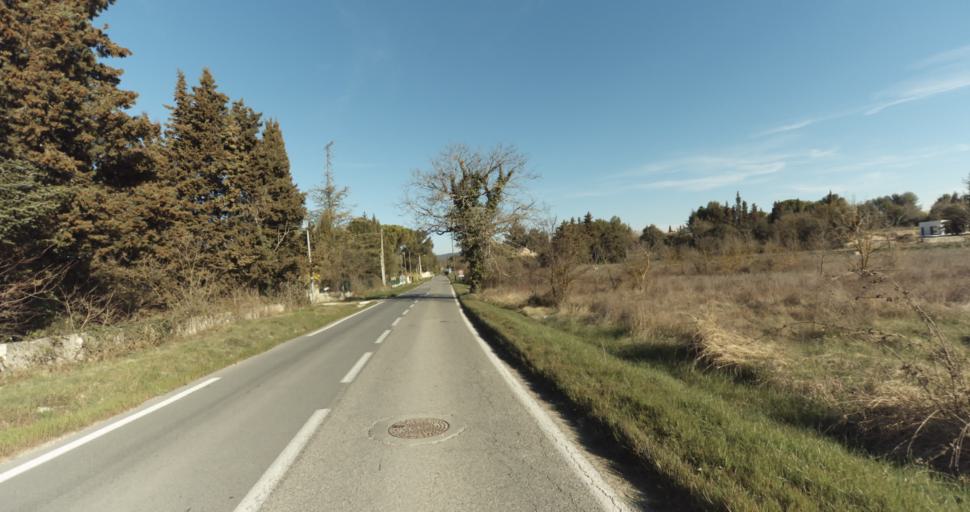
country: FR
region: Provence-Alpes-Cote d'Azur
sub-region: Departement des Bouches-du-Rhone
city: Aix-en-Provence
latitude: 43.5645
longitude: 5.4287
